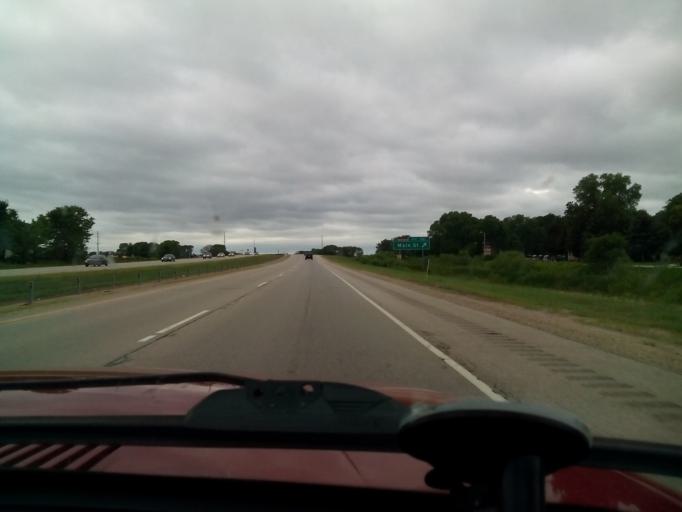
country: US
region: Wisconsin
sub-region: Dane County
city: Sun Prairie
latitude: 43.1793
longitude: -89.2451
